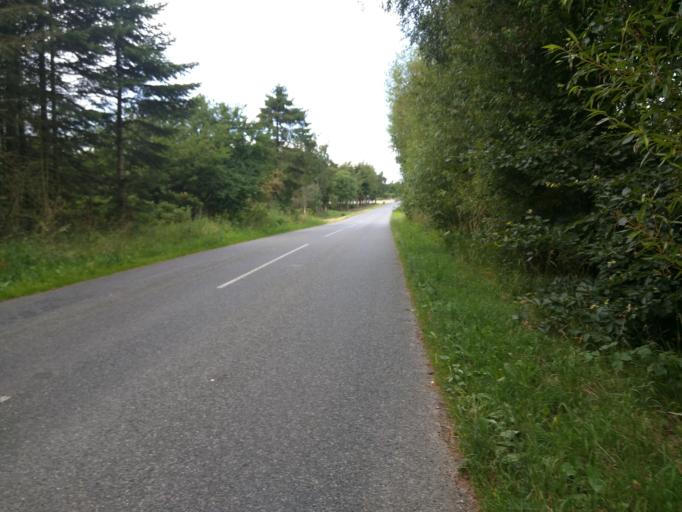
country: DK
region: Zealand
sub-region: Kalundborg Kommune
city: Svebolle
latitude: 55.6803
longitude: 11.3227
